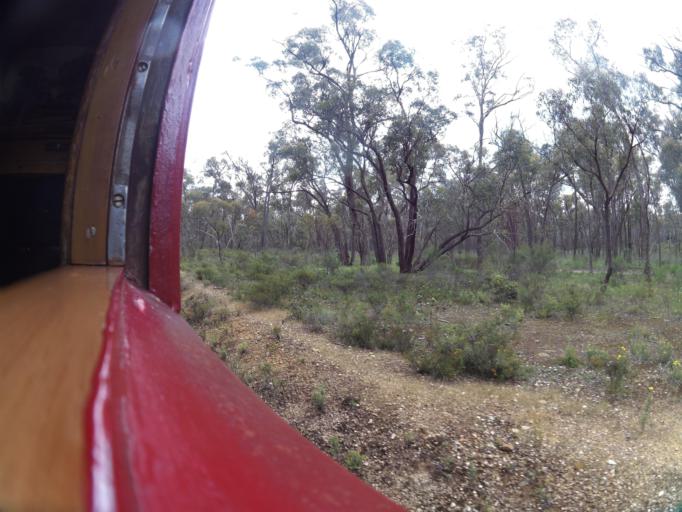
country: AU
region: Victoria
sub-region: Mount Alexander
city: Castlemaine
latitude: -37.0092
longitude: 144.1264
